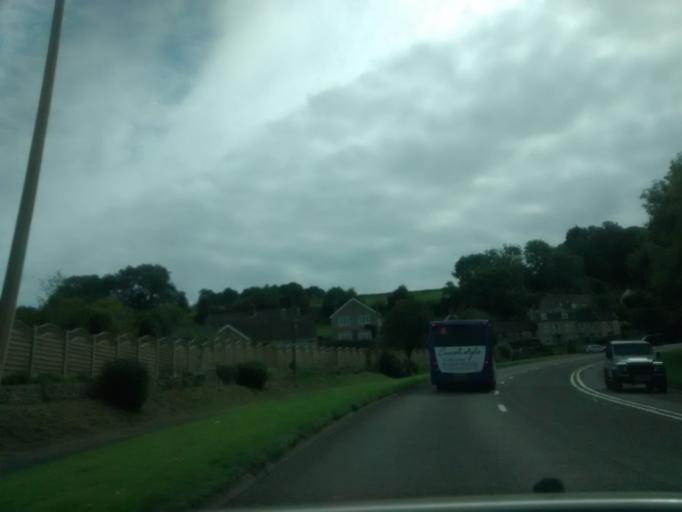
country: GB
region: England
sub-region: South Gloucestershire
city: Horton
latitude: 51.5317
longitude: -2.3544
